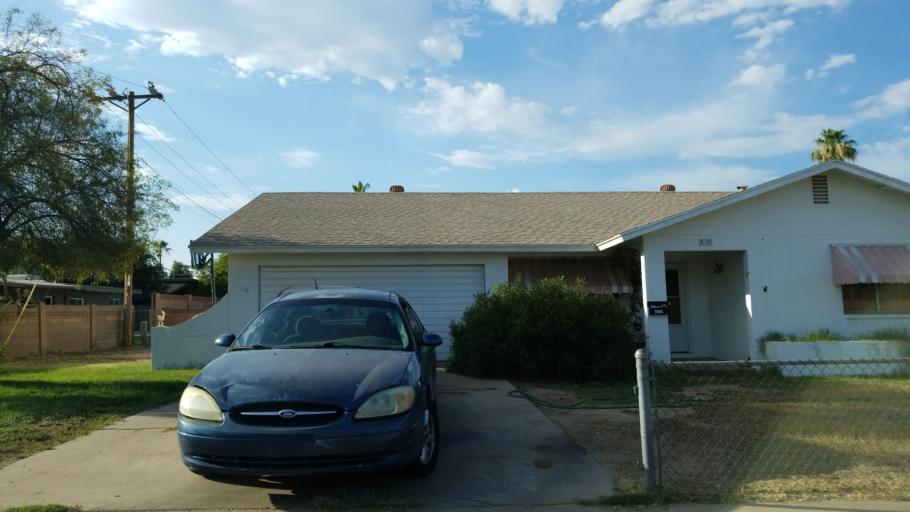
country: US
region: Arizona
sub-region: Maricopa County
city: Scottsdale
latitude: 33.5138
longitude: -111.9047
